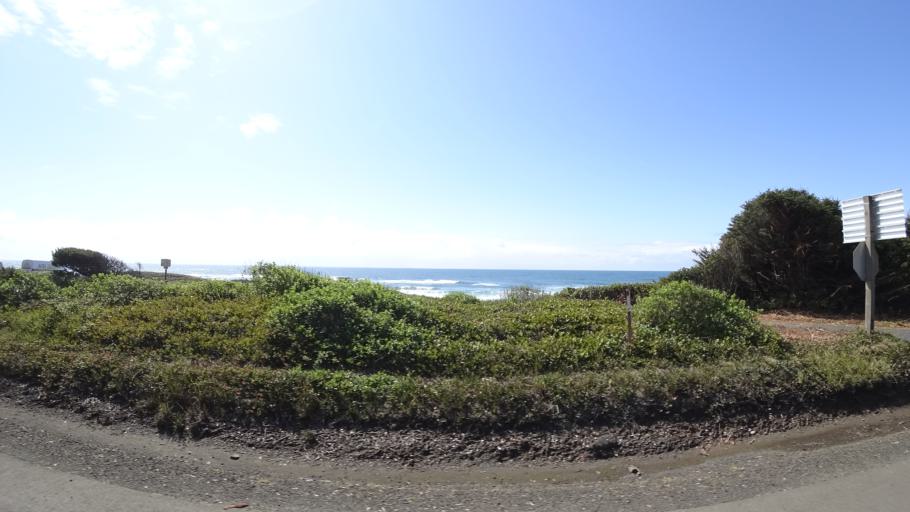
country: US
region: Oregon
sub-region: Lincoln County
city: Newport
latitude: 44.7045
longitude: -124.0608
